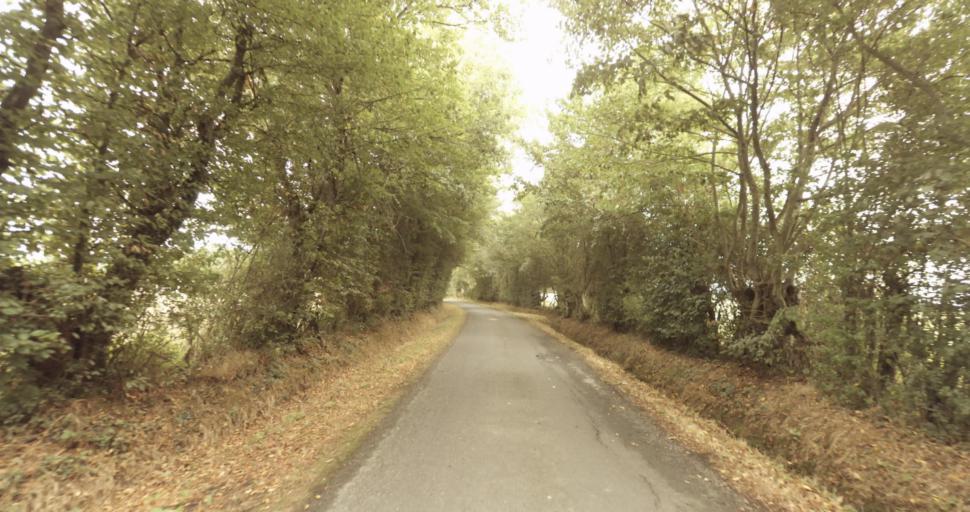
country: FR
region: Lower Normandy
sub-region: Departement de l'Orne
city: Sainte-Gauburge-Sainte-Colombe
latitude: 48.7200
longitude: 0.4891
